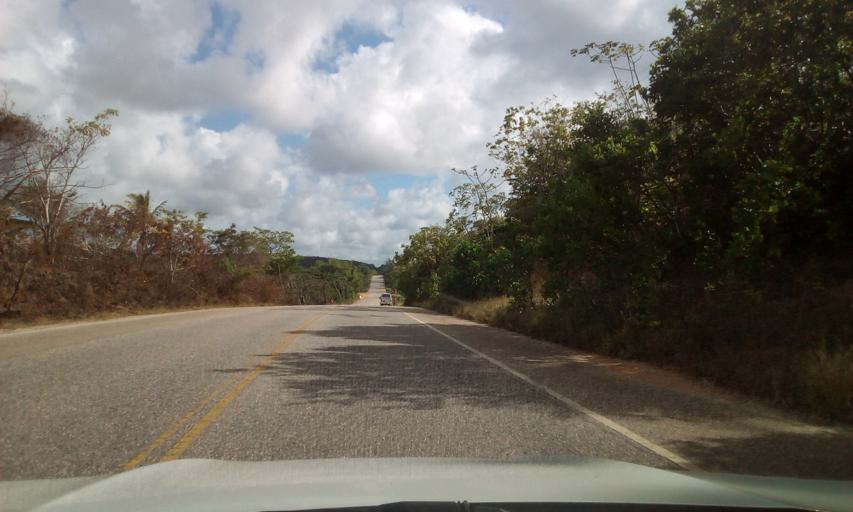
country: BR
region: Sergipe
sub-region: Indiaroba
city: Indiaroba
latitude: -11.4101
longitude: -37.4883
